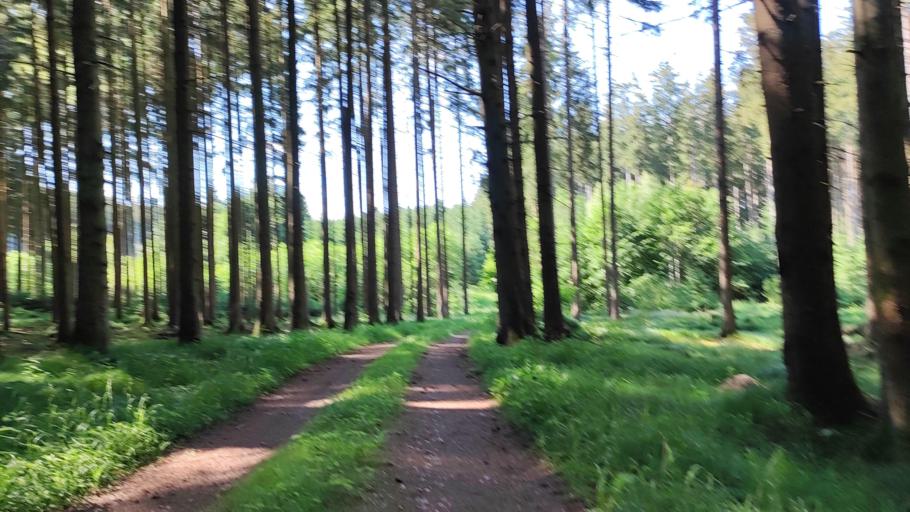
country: DE
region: Bavaria
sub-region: Swabia
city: Burtenbach
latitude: 48.3692
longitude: 10.4971
